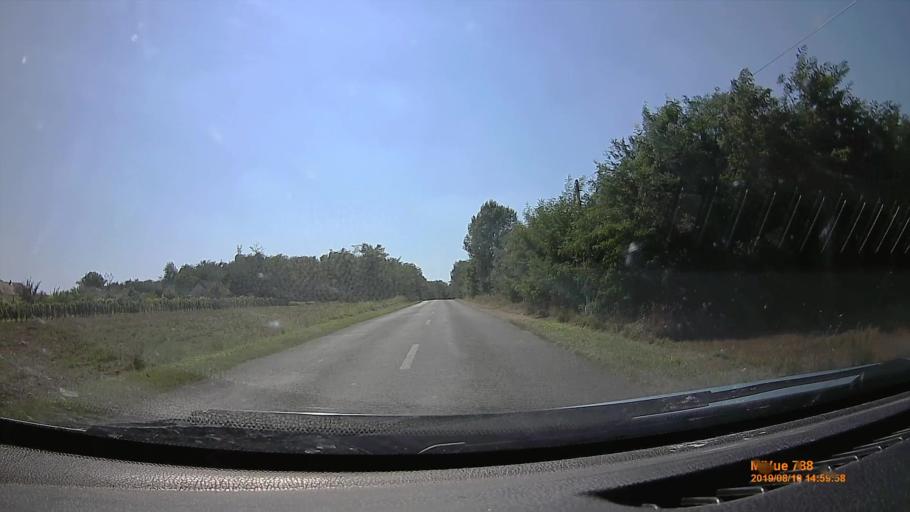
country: HU
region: Somogy
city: Lengyeltoti
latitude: 46.6507
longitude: 17.5905
